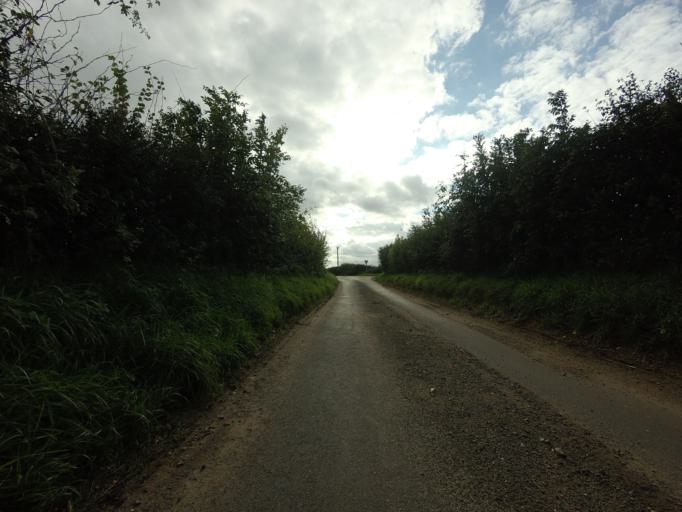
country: GB
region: England
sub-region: Norfolk
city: Snettisham
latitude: 52.8767
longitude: 0.5149
